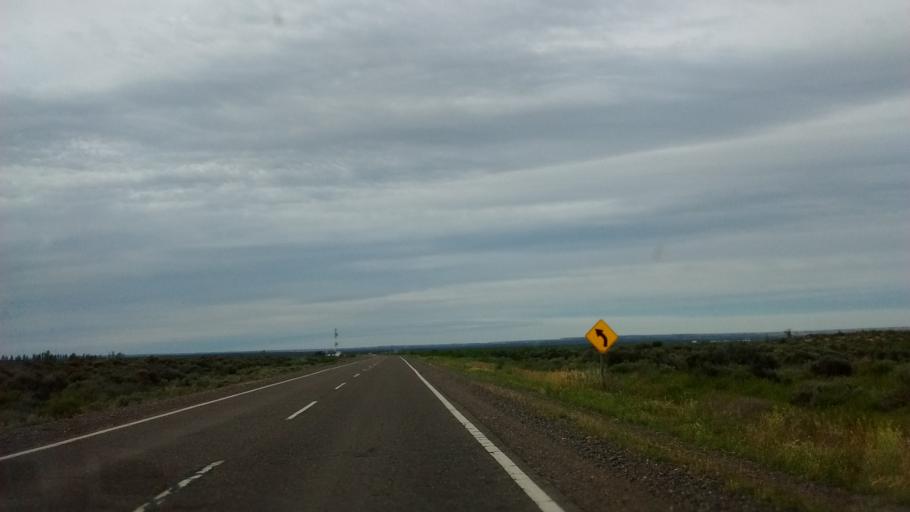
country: AR
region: Rio Negro
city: Catriel
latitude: -38.0185
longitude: -67.9144
